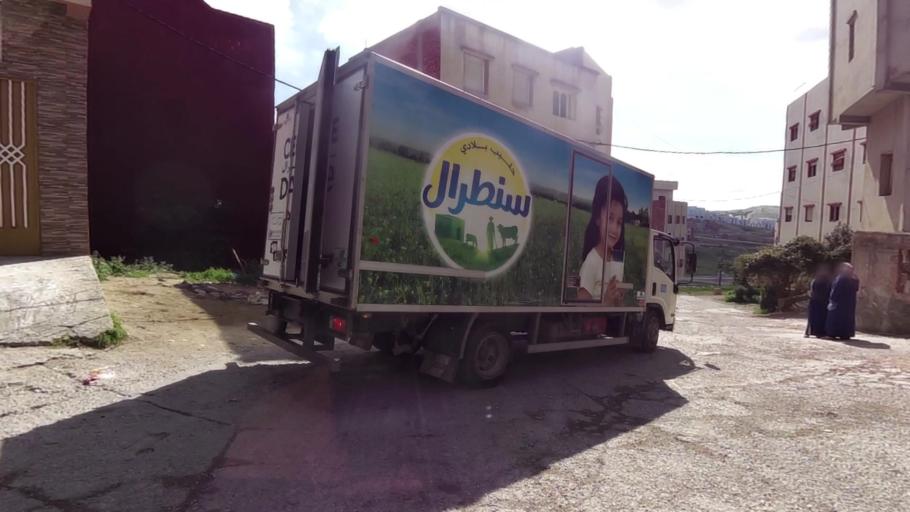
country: MA
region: Tanger-Tetouan
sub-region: Tanger-Assilah
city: Tangier
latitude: 35.7686
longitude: -5.7709
